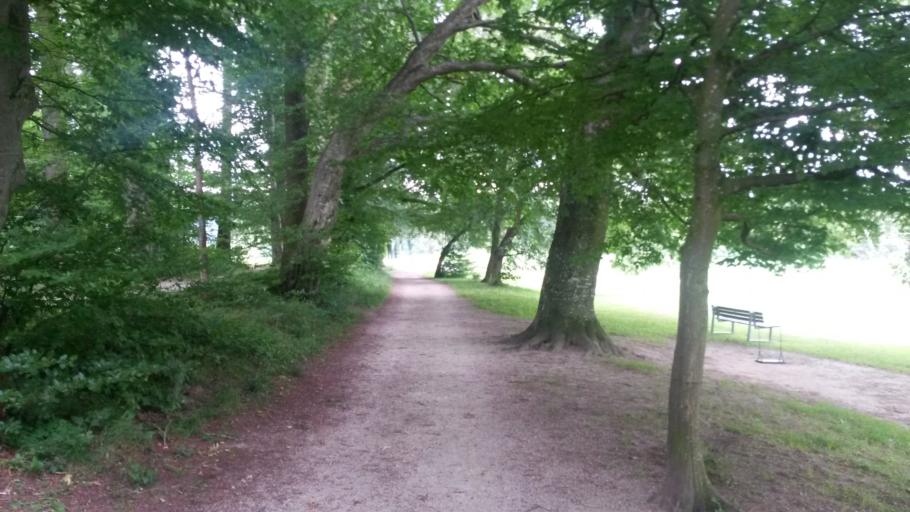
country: DE
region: Bavaria
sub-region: Upper Bavaria
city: Bad Endorf
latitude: 47.9003
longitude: 12.2985
